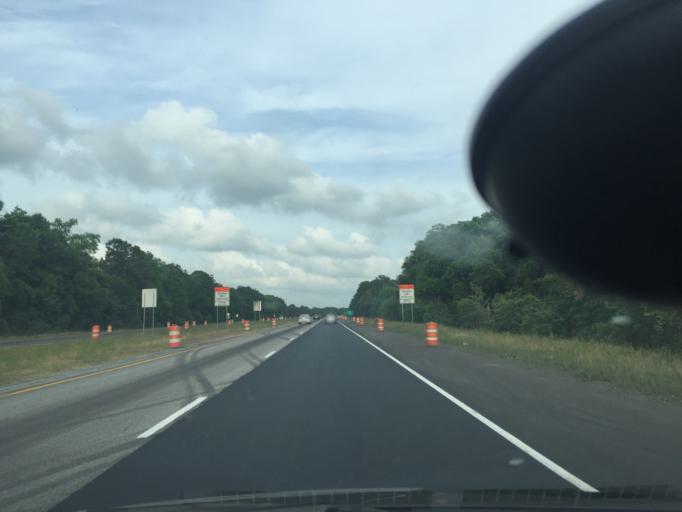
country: US
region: Georgia
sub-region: Chatham County
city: Georgetown
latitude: 32.0015
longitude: -81.2601
